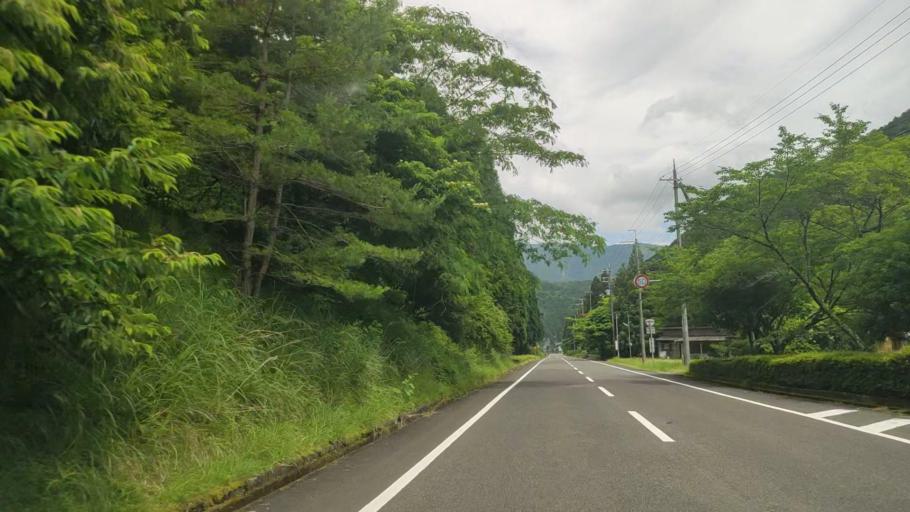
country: JP
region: Kyoto
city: Fukuchiyama
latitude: 35.2310
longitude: 134.9445
